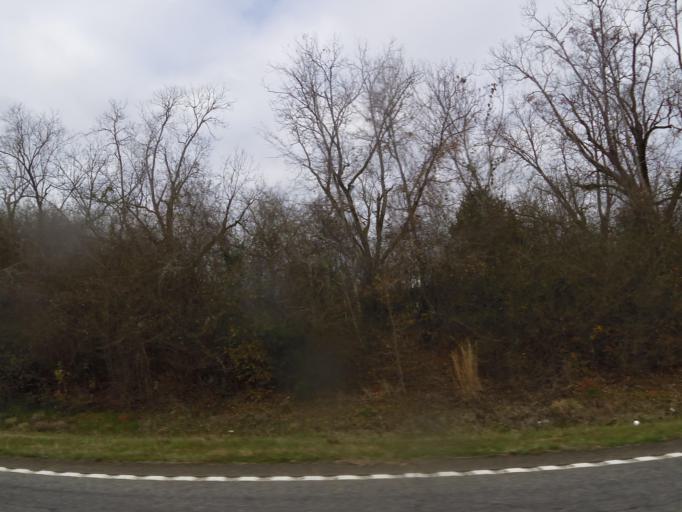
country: US
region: Georgia
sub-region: Quitman County
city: Georgetown
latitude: 31.8580
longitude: -85.0639
